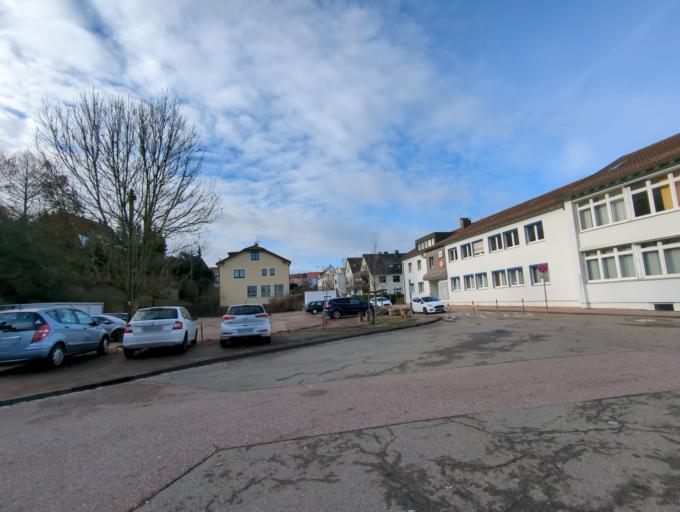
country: DE
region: Baden-Wuerttemberg
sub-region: Regierungsbezirk Stuttgart
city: Schwabisch Gmund
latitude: 48.8001
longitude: 9.8104
